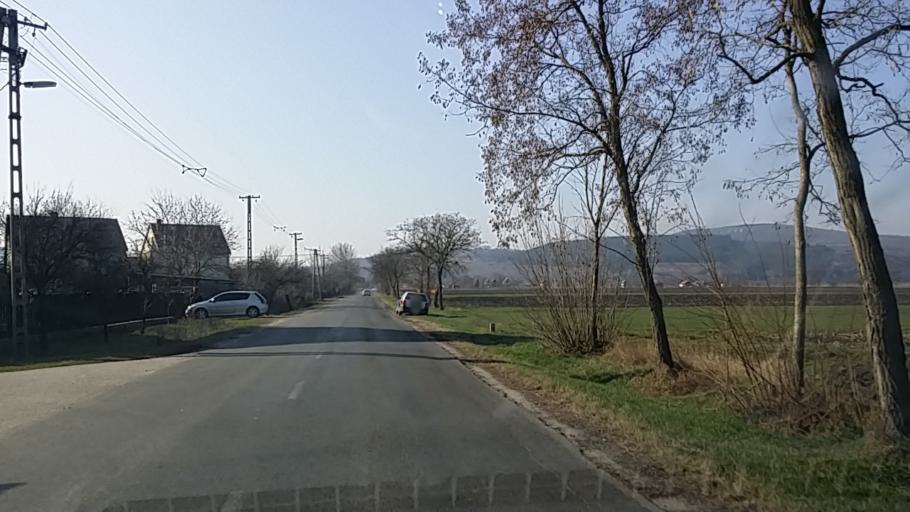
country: HU
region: Komarom-Esztergom
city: Tat
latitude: 47.7395
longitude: 18.6362
